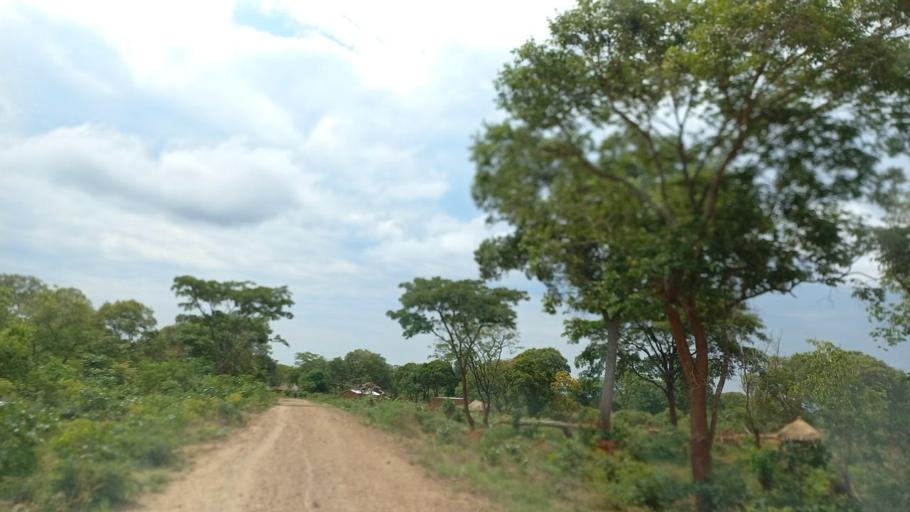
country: ZM
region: North-Western
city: Kalengwa
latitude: -13.4627
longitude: 25.0074
